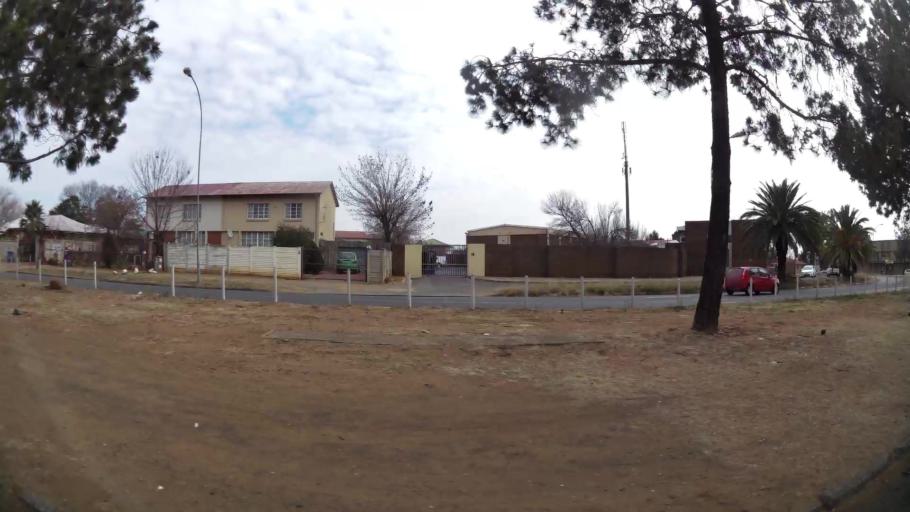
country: ZA
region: Orange Free State
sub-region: Mangaung Metropolitan Municipality
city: Bloemfontein
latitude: -29.1302
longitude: 26.1915
